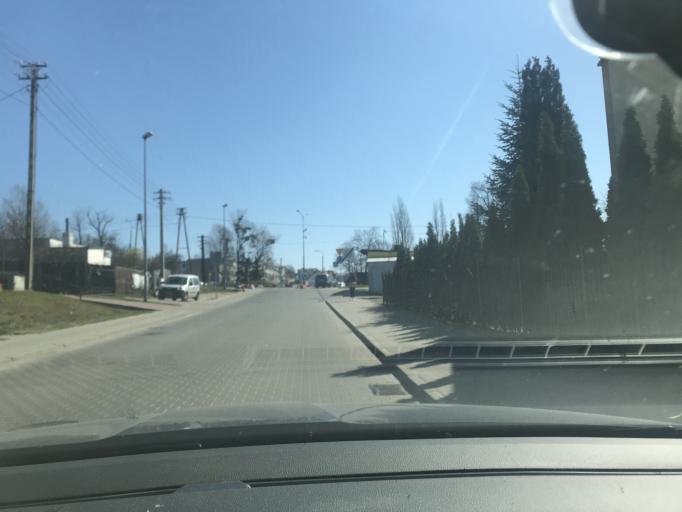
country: PL
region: Pomeranian Voivodeship
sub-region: Gdynia
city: Pogorze
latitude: 54.5587
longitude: 18.4740
